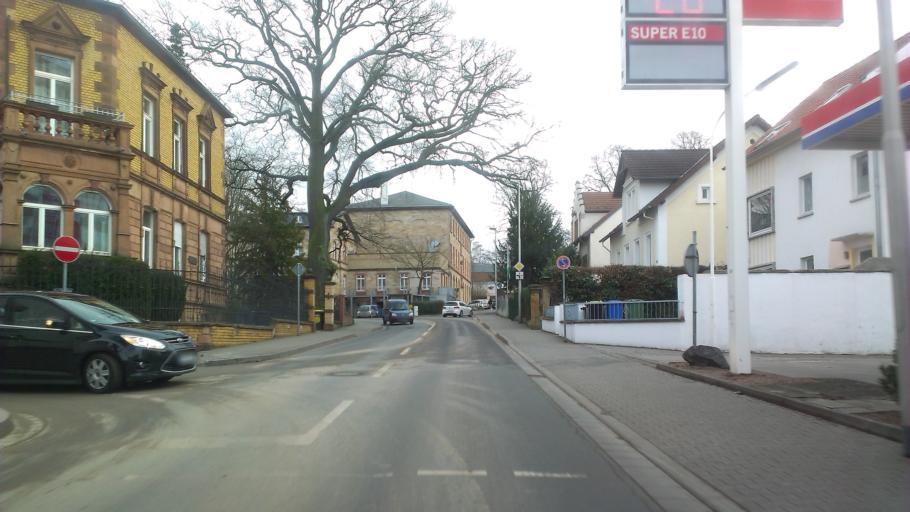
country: DE
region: Rheinland-Pfalz
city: Alzey
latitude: 49.7429
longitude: 8.1081
